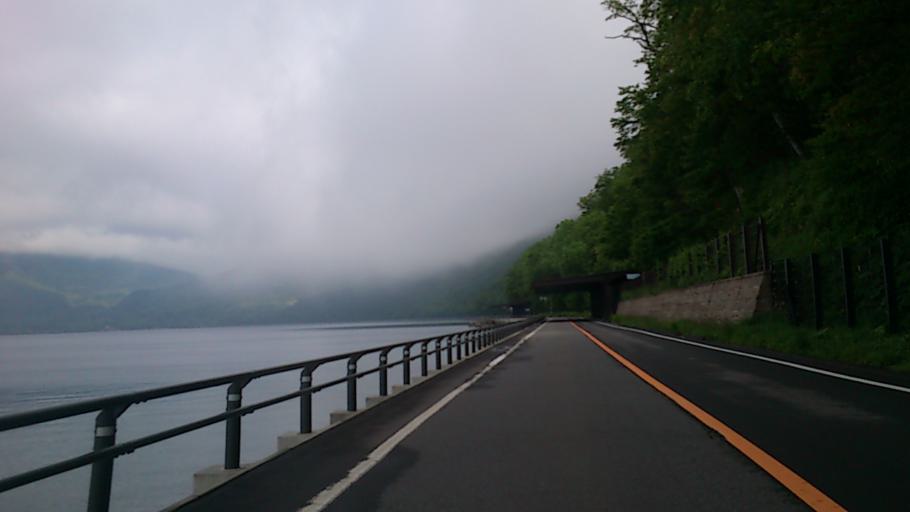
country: JP
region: Hokkaido
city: Shiraoi
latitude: 42.7941
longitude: 141.3676
